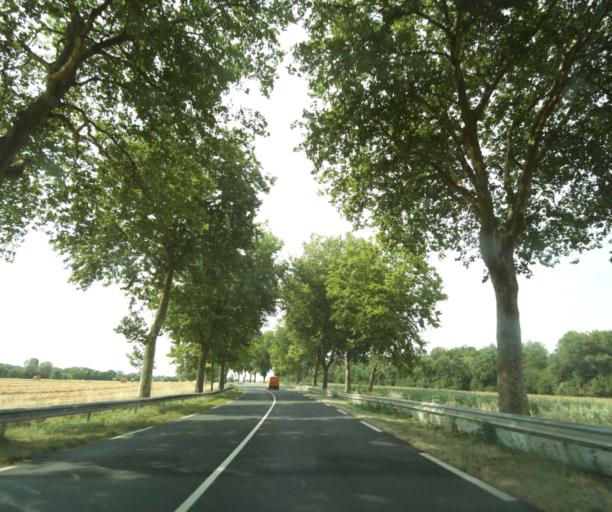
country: FR
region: Centre
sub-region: Departement d'Indre-et-Loire
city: Neuille-Pont-Pierre
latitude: 47.5197
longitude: 0.5841
